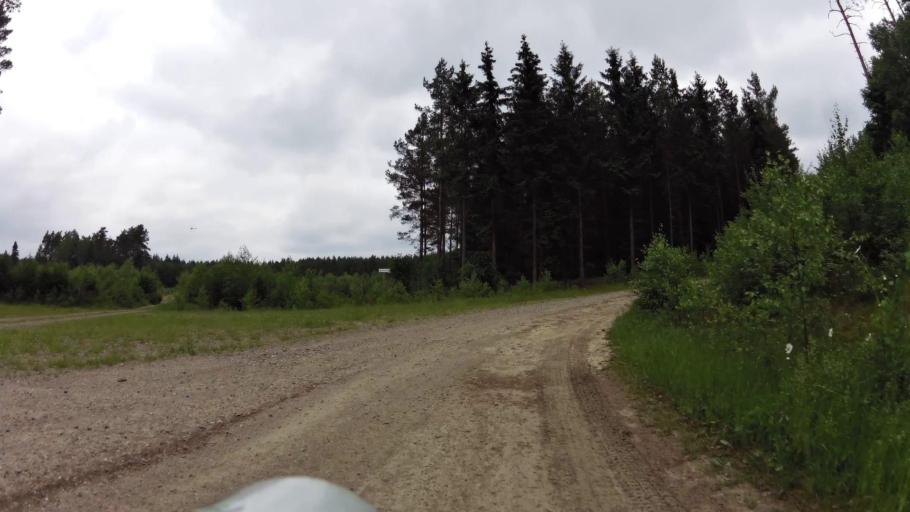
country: PL
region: West Pomeranian Voivodeship
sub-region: Powiat szczecinecki
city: Bialy Bor
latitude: 53.9124
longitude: 16.8307
